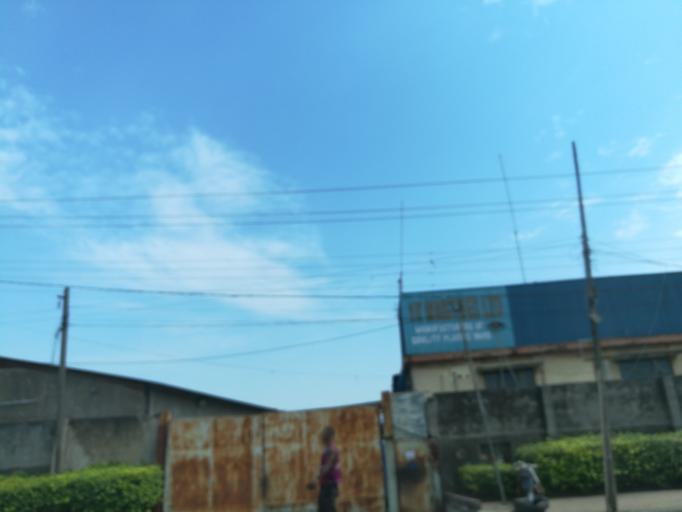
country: NG
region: Lagos
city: Oshodi
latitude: 6.5463
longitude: 3.3284
